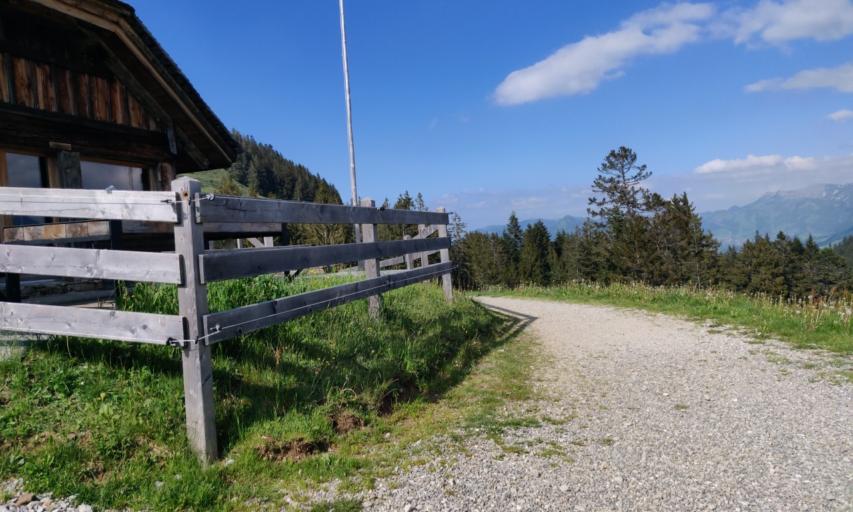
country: CH
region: Fribourg
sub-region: Gruyere District
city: Vuadens
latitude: 46.5726
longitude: 7.0244
